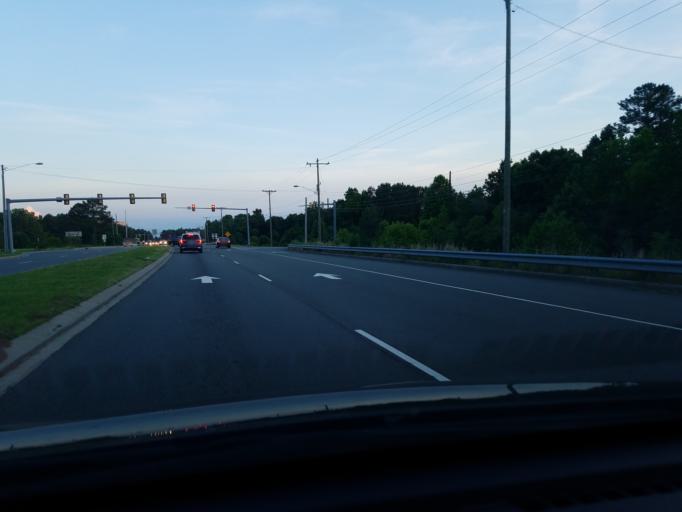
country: US
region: North Carolina
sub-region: Orange County
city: Chapel Hill
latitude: 35.9060
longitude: -78.9603
